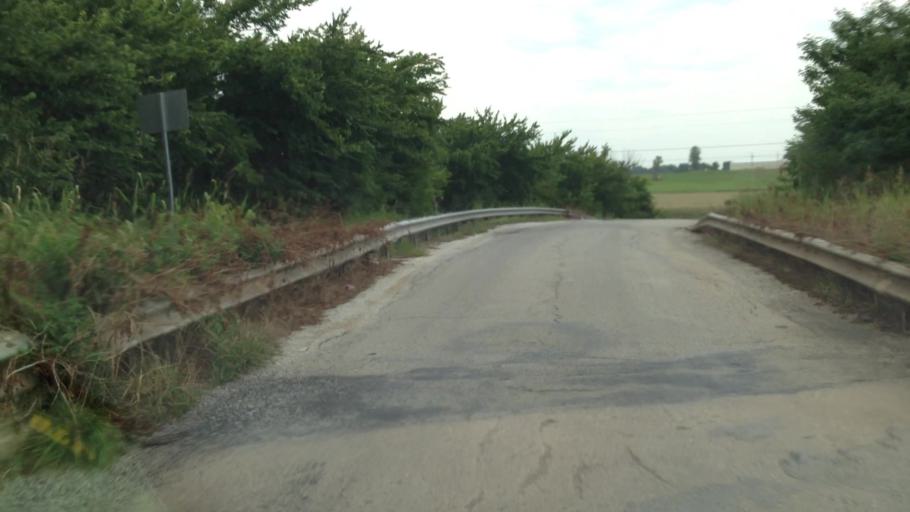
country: US
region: Oklahoma
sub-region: Craig County
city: Vinita
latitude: 36.6386
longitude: -95.1254
